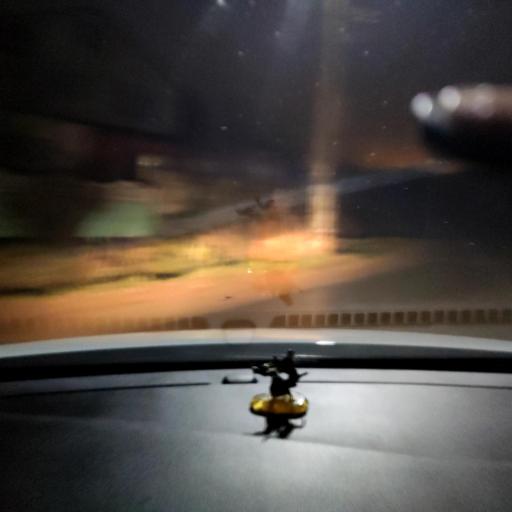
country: RU
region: Tatarstan
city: Vysokaya Gora
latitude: 55.7990
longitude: 49.4040
